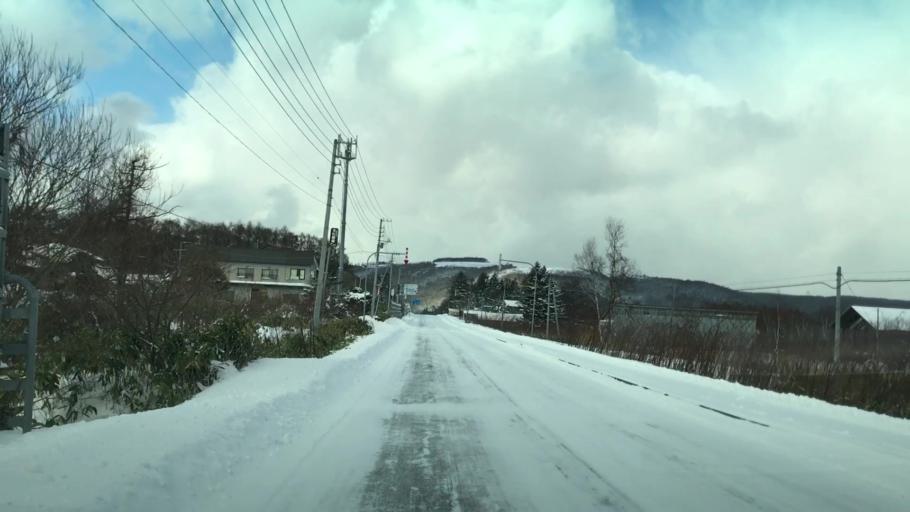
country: JP
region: Hokkaido
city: Yoichi
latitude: 43.3110
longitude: 140.5483
